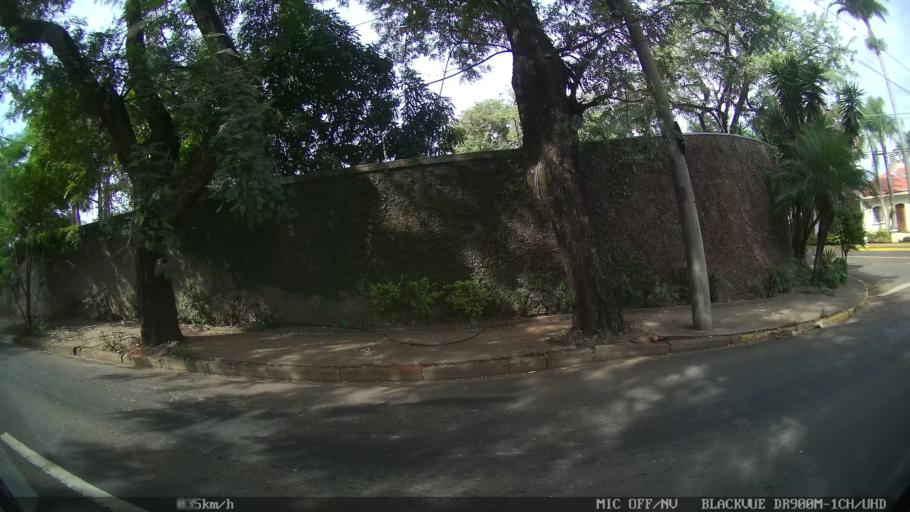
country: BR
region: Sao Paulo
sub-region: Piracicaba
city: Piracicaba
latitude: -22.7233
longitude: -47.6654
